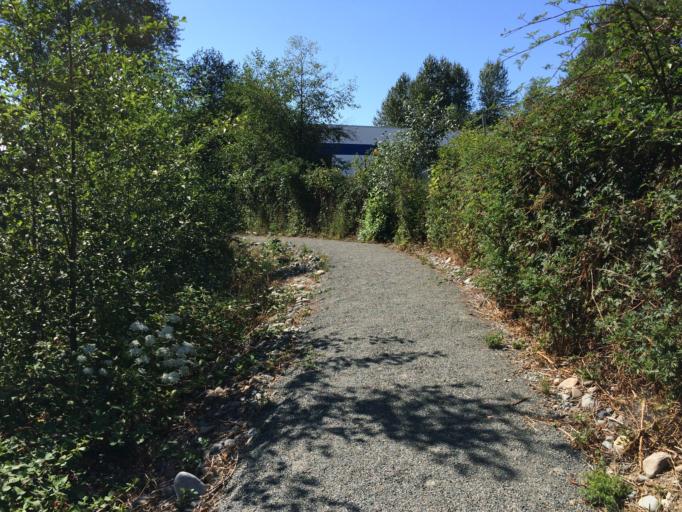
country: CA
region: British Columbia
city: Duncan
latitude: 48.7594
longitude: -123.6873
